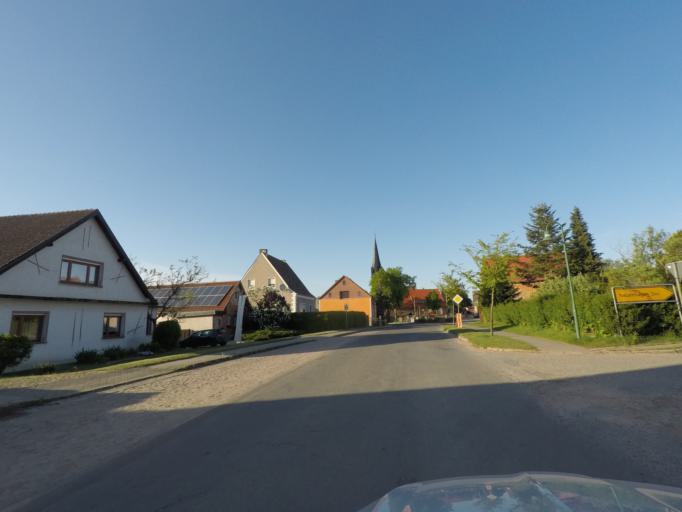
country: DE
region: Brandenburg
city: Liepe
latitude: 52.8346
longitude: 14.0052
